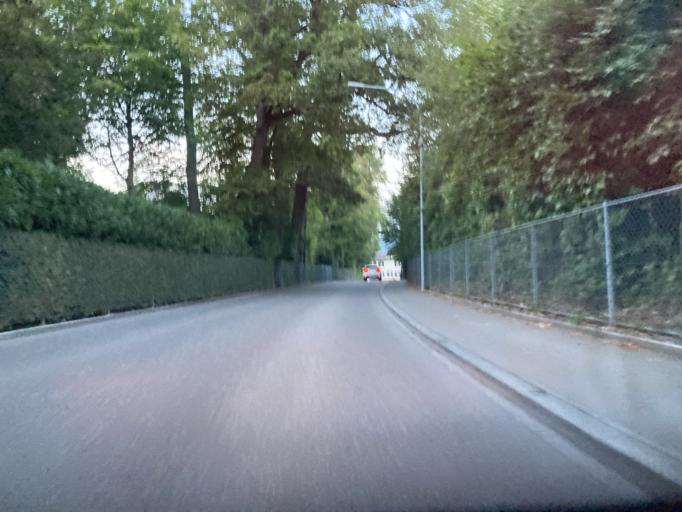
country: CH
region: Zurich
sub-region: Bezirk Horgen
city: Kilchberg / Kilchberg (Dorfkern)
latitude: 47.3146
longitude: 8.5465
